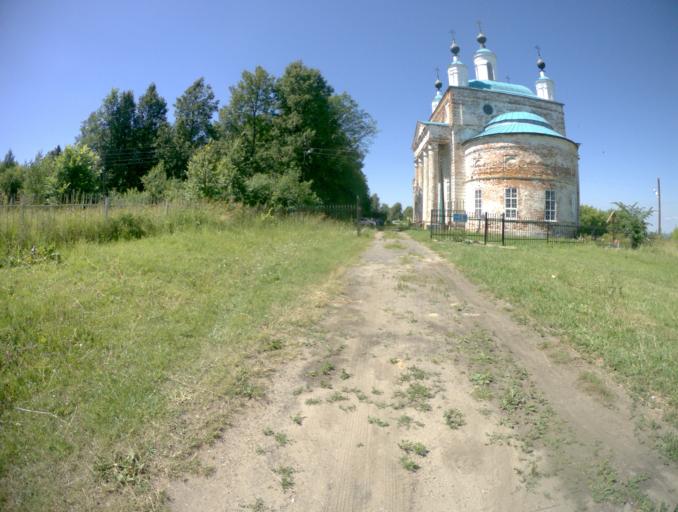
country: RU
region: Nizjnij Novgorod
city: Gorbatov
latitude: 56.1330
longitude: 43.0601
